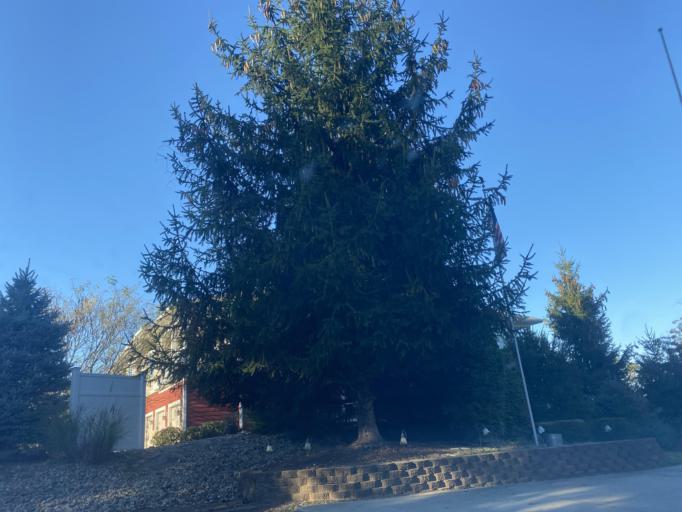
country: US
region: Kentucky
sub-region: Campbell County
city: Dayton
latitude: 39.1092
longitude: -84.4625
